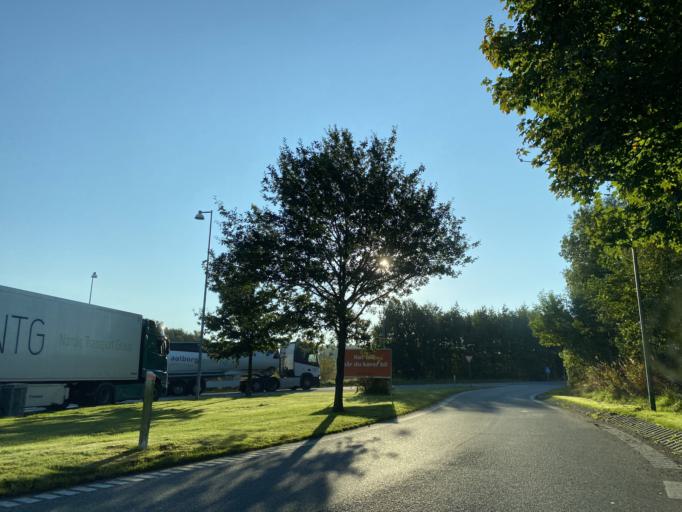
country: DK
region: South Denmark
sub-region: Vejle Kommune
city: Vejle
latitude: 55.6416
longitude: 9.5592
